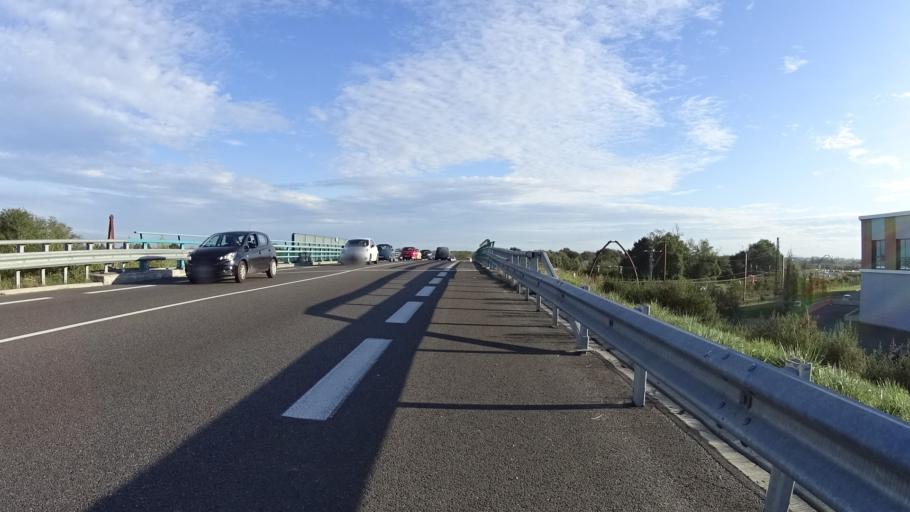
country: FR
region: Aquitaine
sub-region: Departement des Landes
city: Saint-Paul-les-Dax
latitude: 43.7282
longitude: -1.0368
